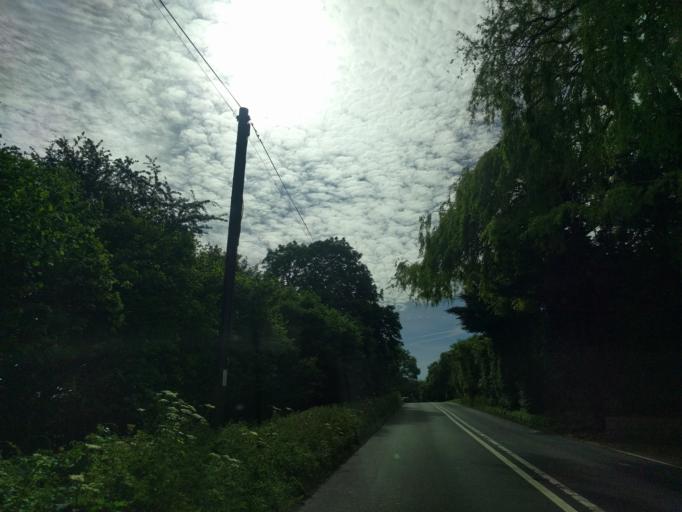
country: GB
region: England
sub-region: Wiltshire
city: Seend
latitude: 51.3372
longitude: -2.1218
